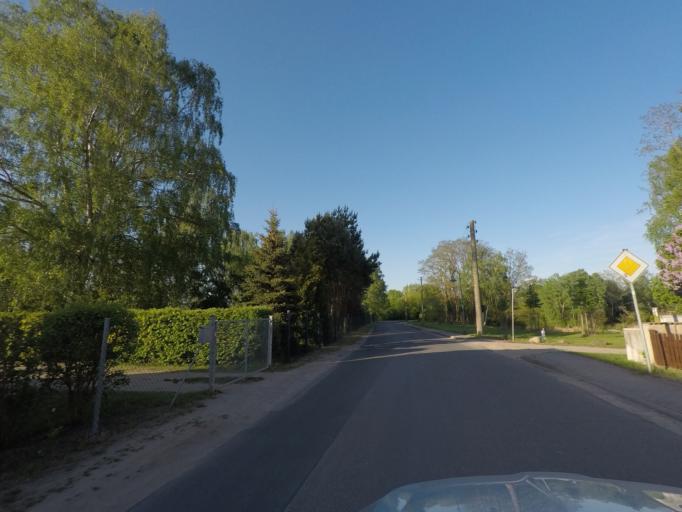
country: DE
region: Brandenburg
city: Oderberg
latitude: 52.8384
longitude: 14.0092
